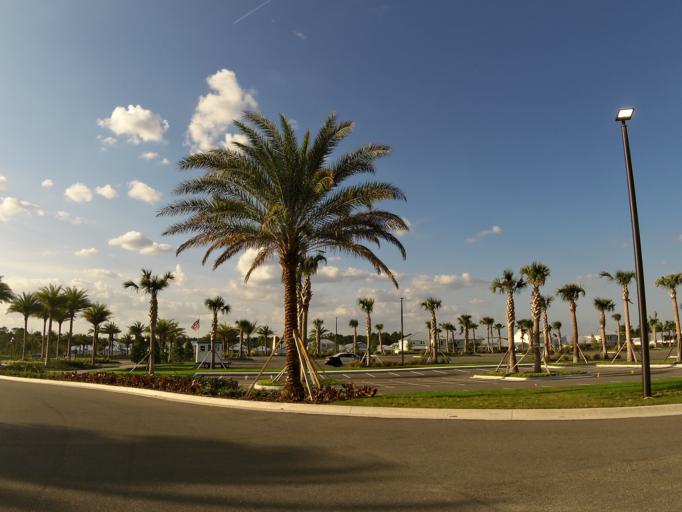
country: US
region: Florida
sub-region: Saint Johns County
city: Palm Valley
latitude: 30.0839
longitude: -81.4836
